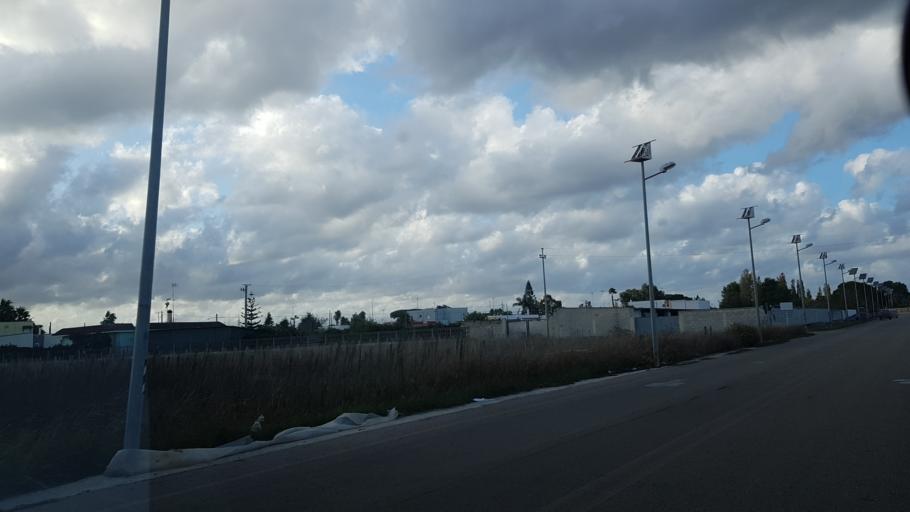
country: IT
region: Apulia
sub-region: Provincia di Brindisi
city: San Pietro Vernotico
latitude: 40.4956
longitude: 18.0075
